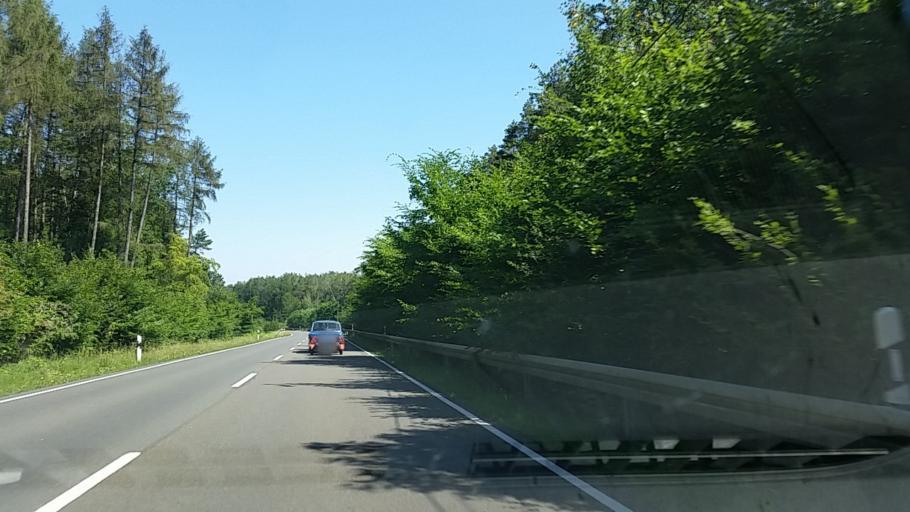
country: DE
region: Saxony-Anhalt
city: Kemberg
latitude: 51.7074
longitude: 12.6185
